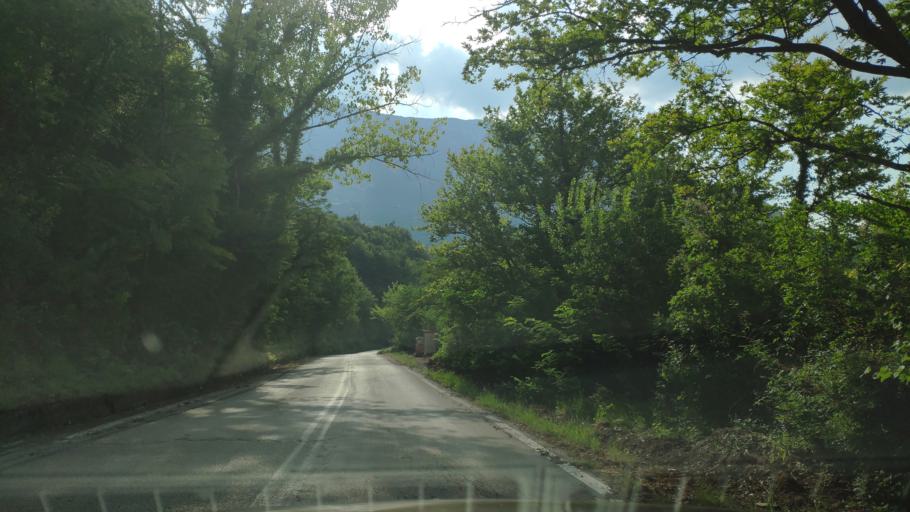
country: GR
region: Epirus
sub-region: Nomos Artas
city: Agios Dimitrios
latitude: 39.4574
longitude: 21.0446
